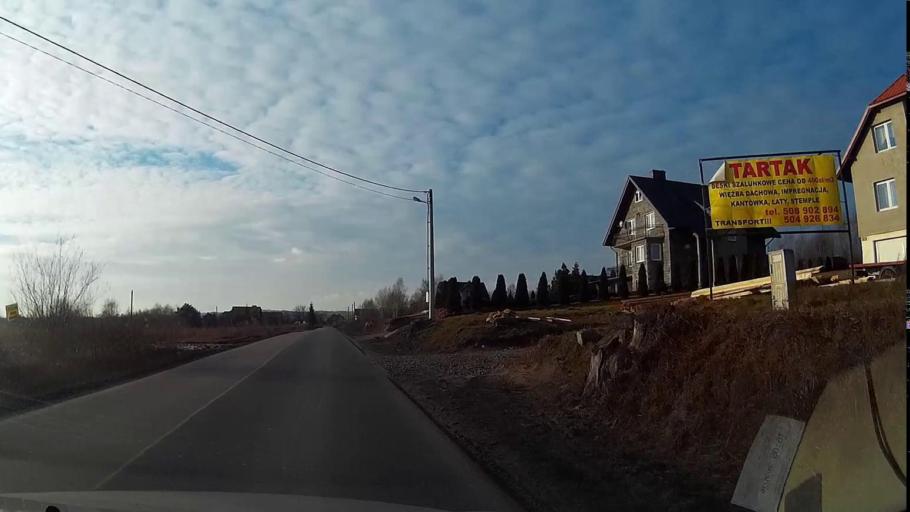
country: PL
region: Lesser Poland Voivodeship
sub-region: Powiat krakowski
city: Mnikow
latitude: 50.0592
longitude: 19.7486
